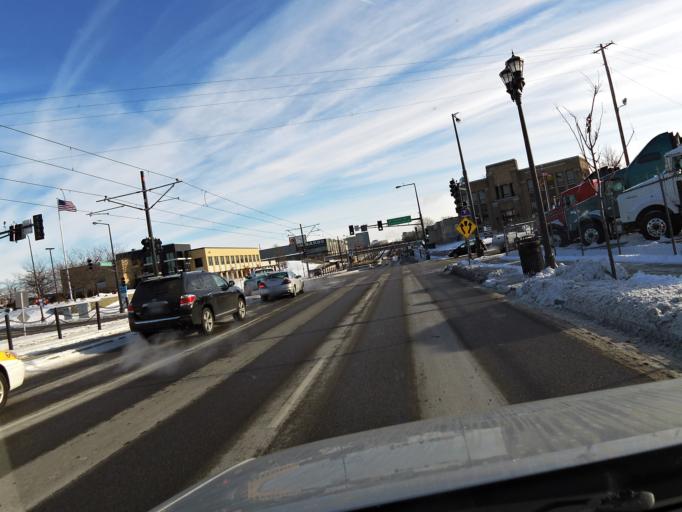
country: US
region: Minnesota
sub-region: Ramsey County
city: Falcon Heights
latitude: 44.9599
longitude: -93.1878
